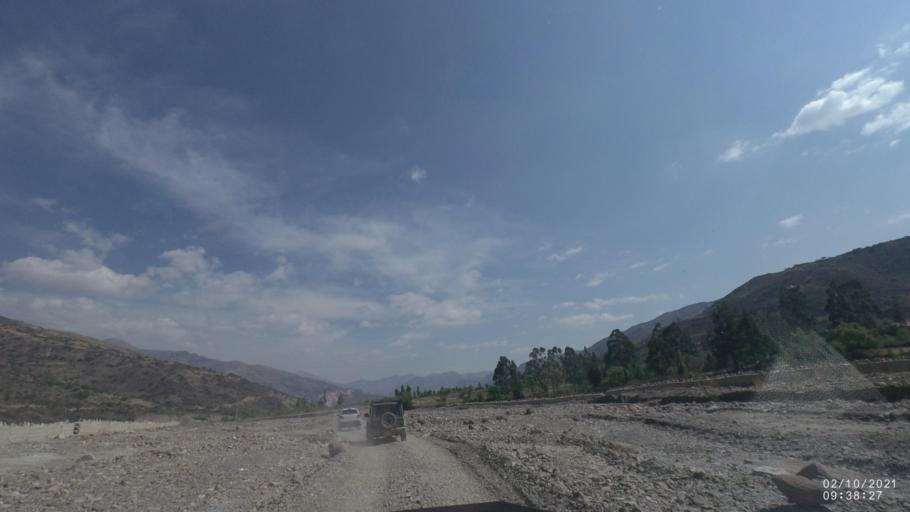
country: BO
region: Cochabamba
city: Irpa Irpa
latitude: -17.8280
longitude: -66.3253
